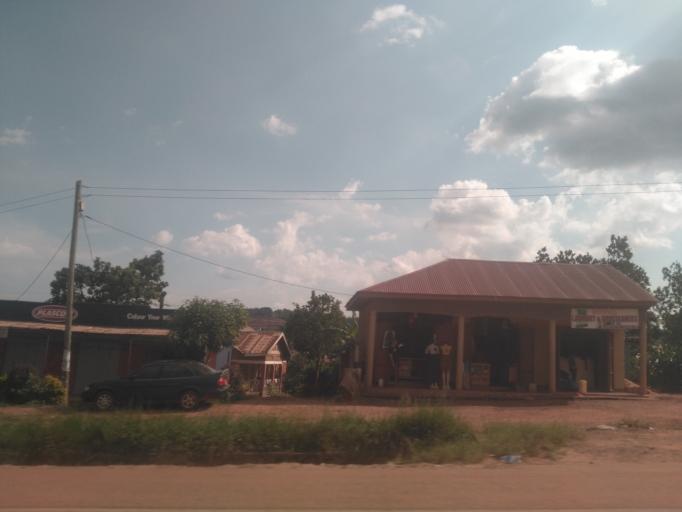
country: UG
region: Central Region
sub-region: Wakiso District
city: Kajansi
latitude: 0.2786
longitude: 32.4804
